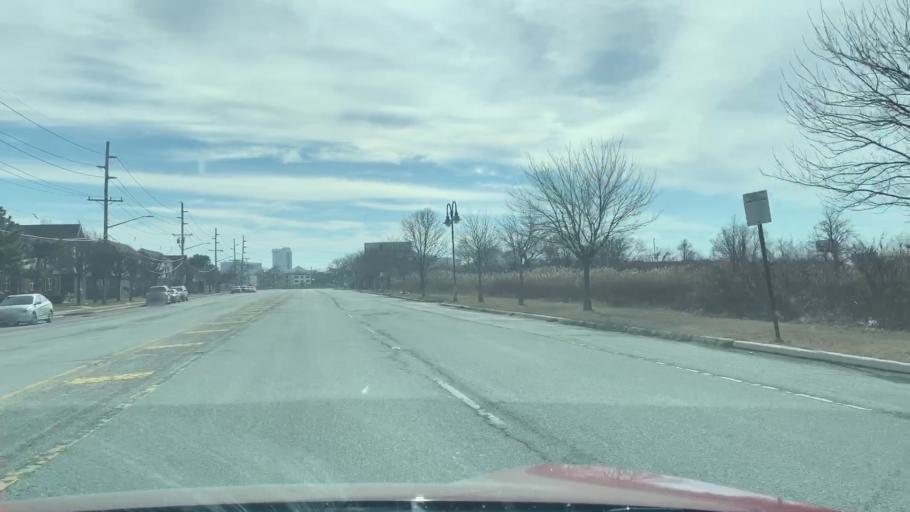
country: US
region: New Jersey
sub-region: Atlantic County
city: Atlantic City
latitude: 39.3747
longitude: -74.4316
